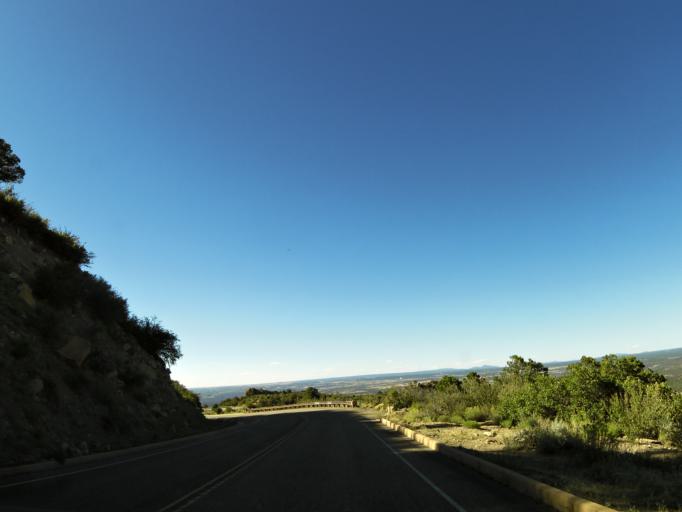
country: US
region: Colorado
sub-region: Montezuma County
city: Mancos
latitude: 37.3177
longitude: -108.4153
